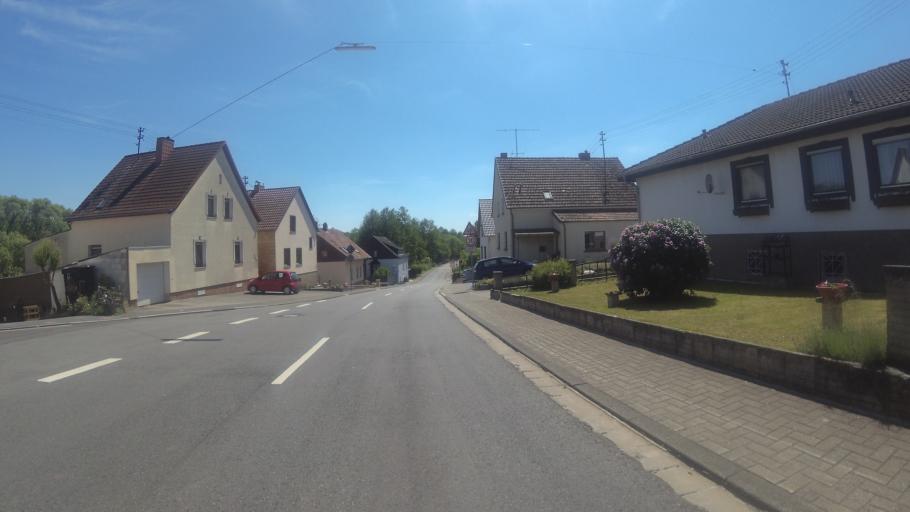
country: DE
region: Saarland
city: Heusweiler
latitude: 49.3633
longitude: 6.9375
